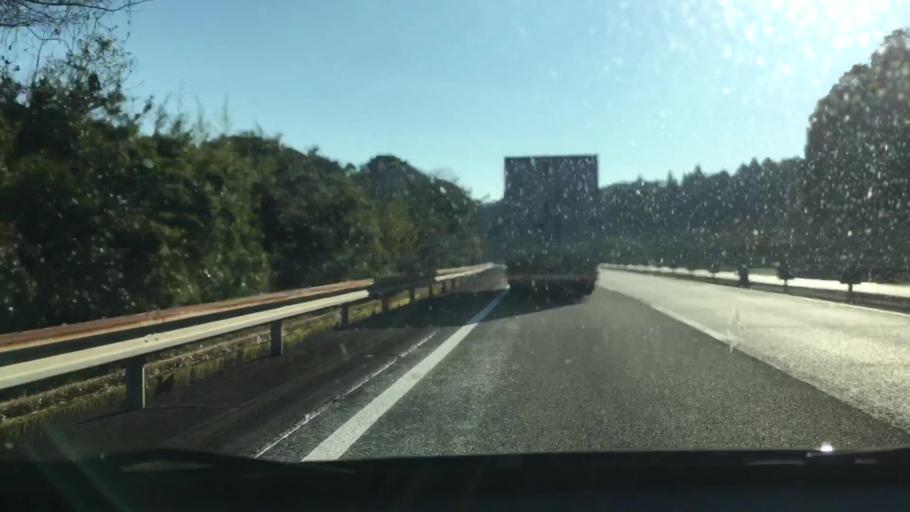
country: JP
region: Kagoshima
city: Kajiki
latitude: 31.8903
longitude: 130.6976
